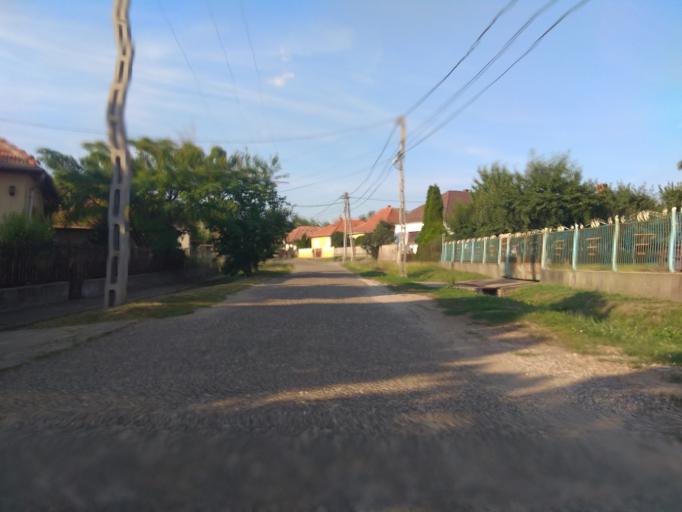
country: HU
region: Borsod-Abauj-Zemplen
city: Harsany
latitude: 47.9240
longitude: 20.7392
